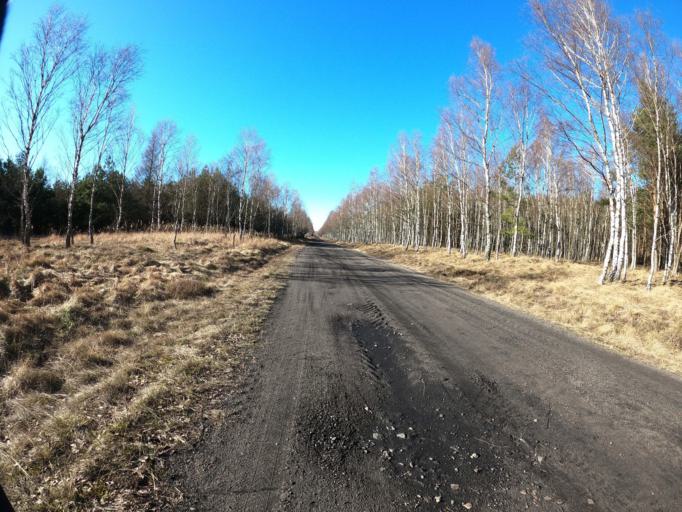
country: PL
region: West Pomeranian Voivodeship
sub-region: Powiat szczecinecki
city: Borne Sulinowo
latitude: 53.5444
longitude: 16.5690
